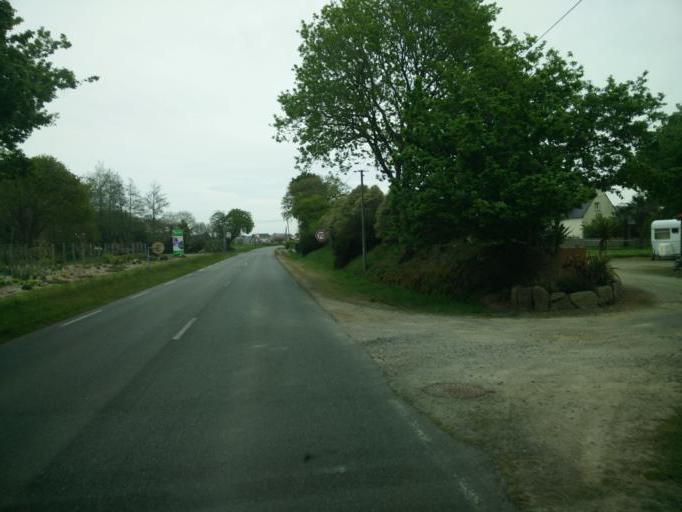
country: FR
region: Brittany
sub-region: Departement des Cotes-d'Armor
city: Pleumeur-Bodou
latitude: 48.7520
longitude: -3.5002
